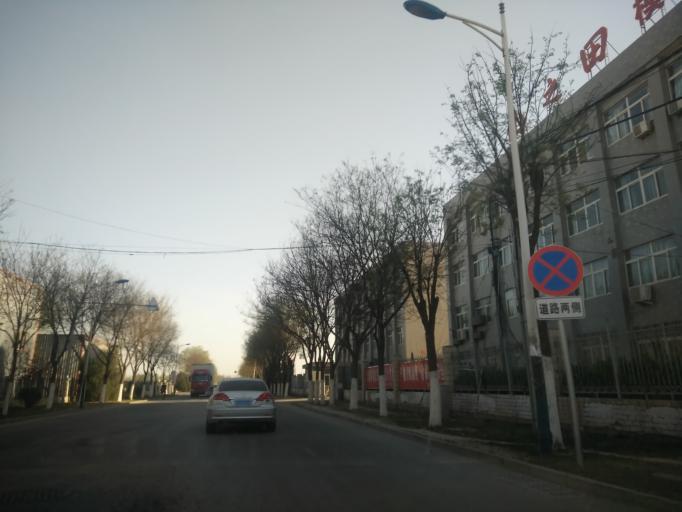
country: CN
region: Beijing
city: Yinghai
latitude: 39.7460
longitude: 116.4421
